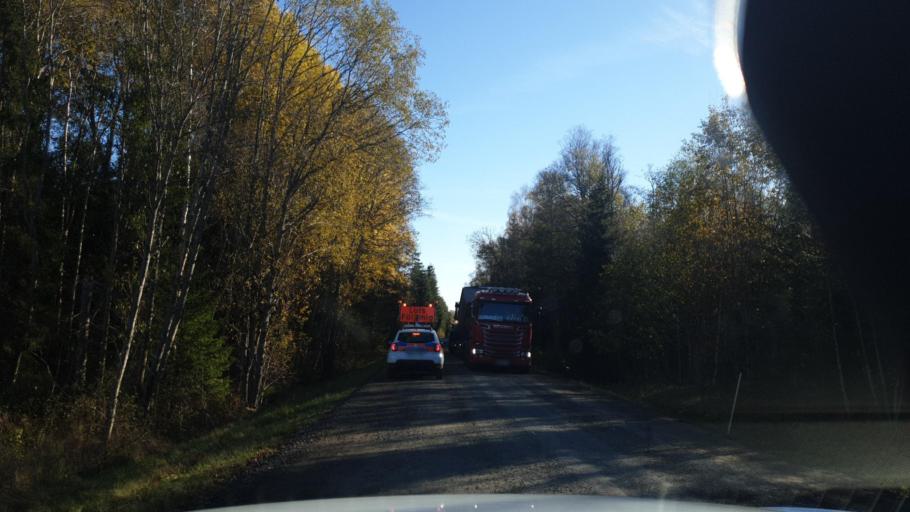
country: SE
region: Vaermland
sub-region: Karlstads Kommun
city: Valberg
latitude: 59.4130
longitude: 13.1677
